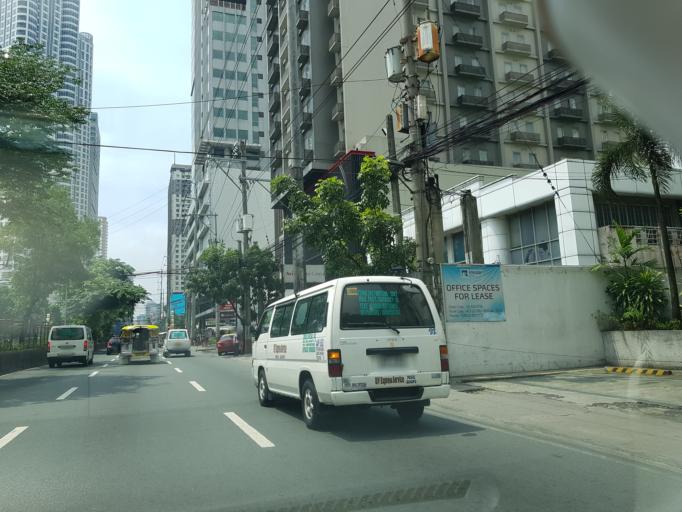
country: PH
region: Metro Manila
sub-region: Pasig
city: Pasig City
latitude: 14.5774
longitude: 121.0583
